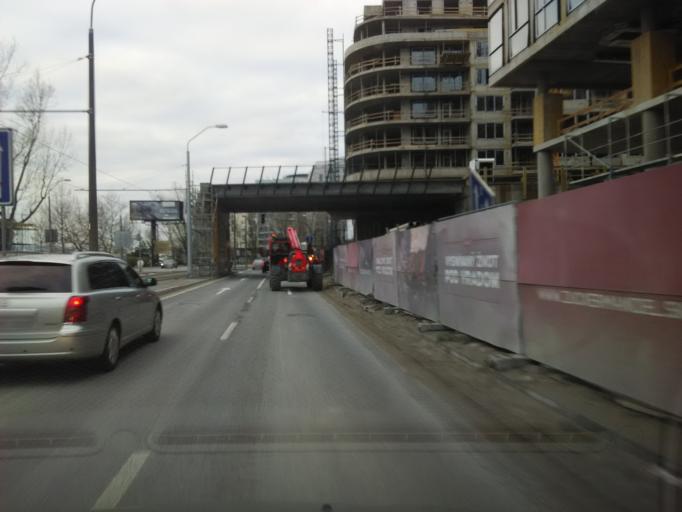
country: SK
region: Bratislavsky
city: Bratislava
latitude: 48.1404
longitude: 17.0951
